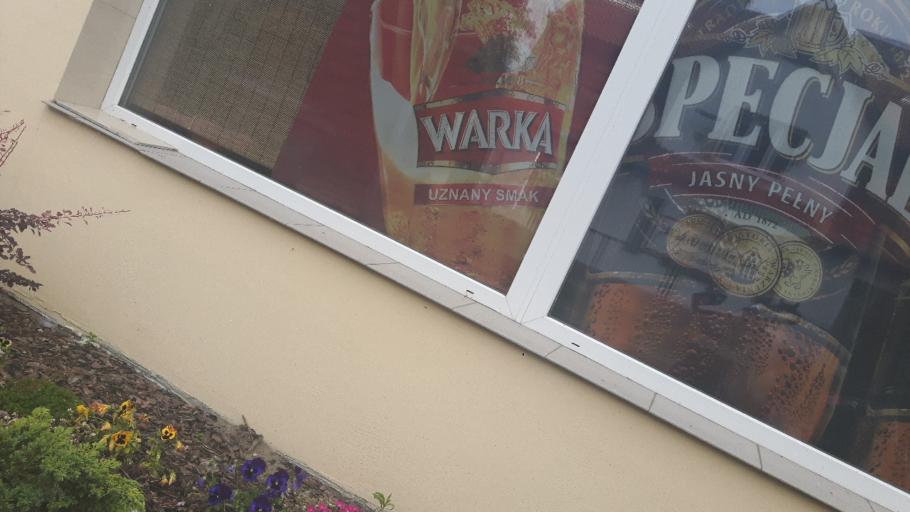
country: PL
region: Pomeranian Voivodeship
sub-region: Powiat nowodworski
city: Krynica Morska
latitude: 54.2842
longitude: 19.4373
